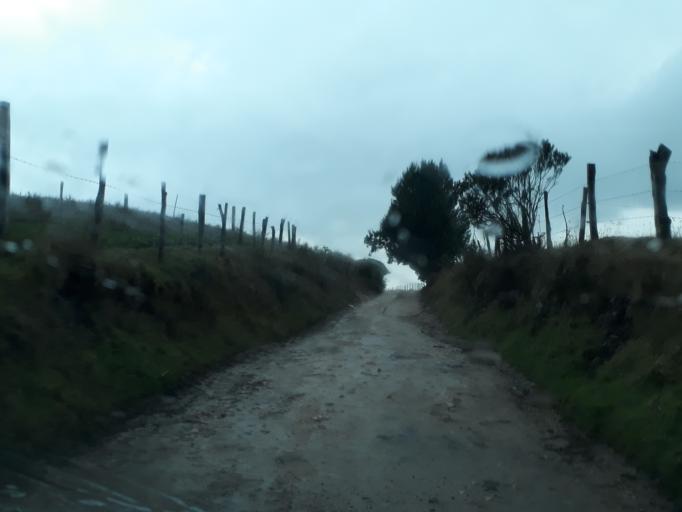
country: CO
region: Cundinamarca
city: Villapinzon
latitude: 5.3022
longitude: -73.5950
